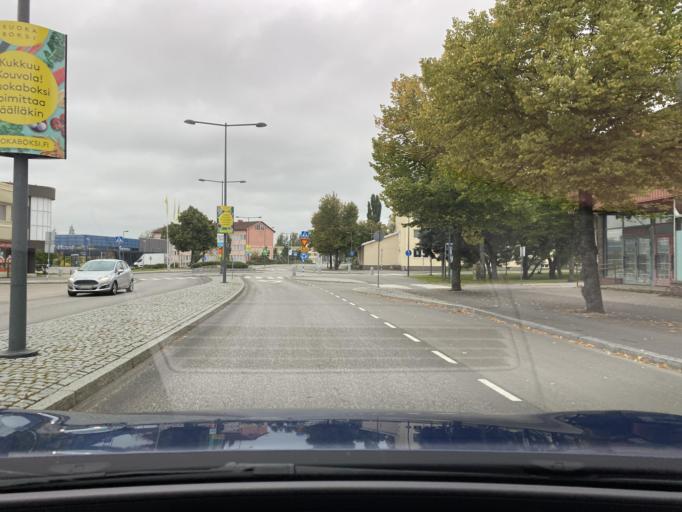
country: FI
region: Kymenlaakso
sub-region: Kouvola
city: Kouvola
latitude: 60.9075
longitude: 26.6223
